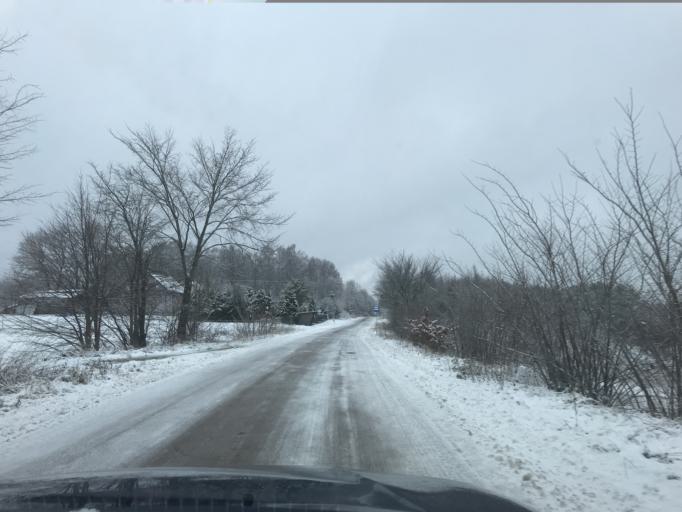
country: PL
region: Pomeranian Voivodeship
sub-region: Powiat bytowski
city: Bytow
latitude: 54.2209
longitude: 17.5630
